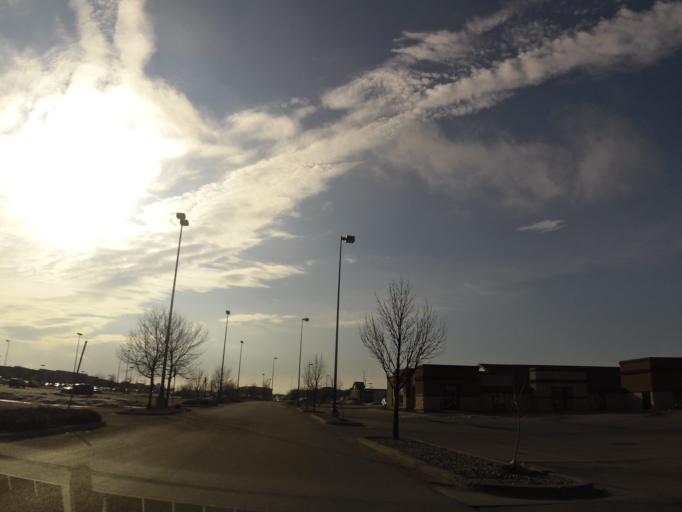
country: US
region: North Dakota
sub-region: Grand Forks County
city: Grand Forks
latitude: 47.8883
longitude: -97.0751
